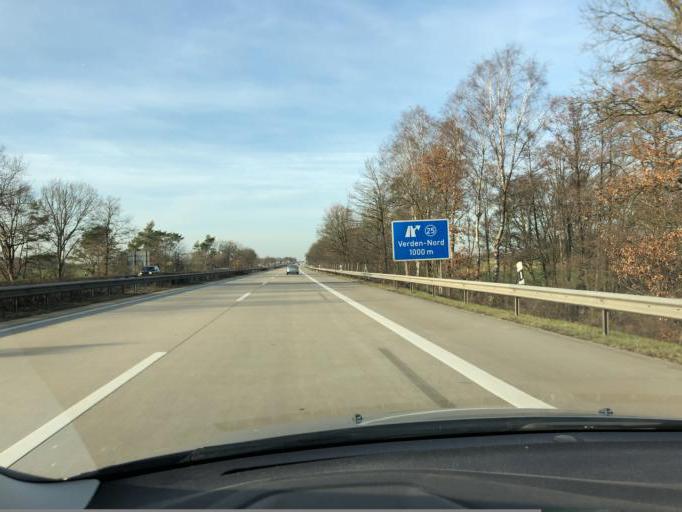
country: DE
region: Lower Saxony
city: Verden
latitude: 52.9470
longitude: 9.2583
